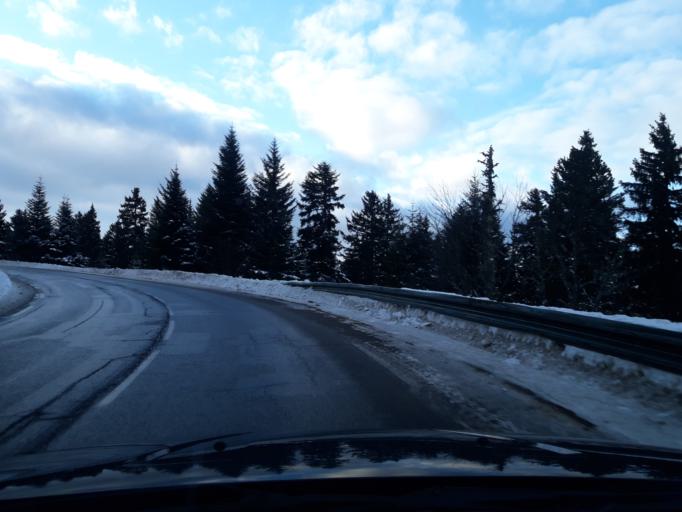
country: FR
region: Rhone-Alpes
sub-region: Departement de l'Isere
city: Vaulnaveys-le-Bas
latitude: 45.1161
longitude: 5.8729
